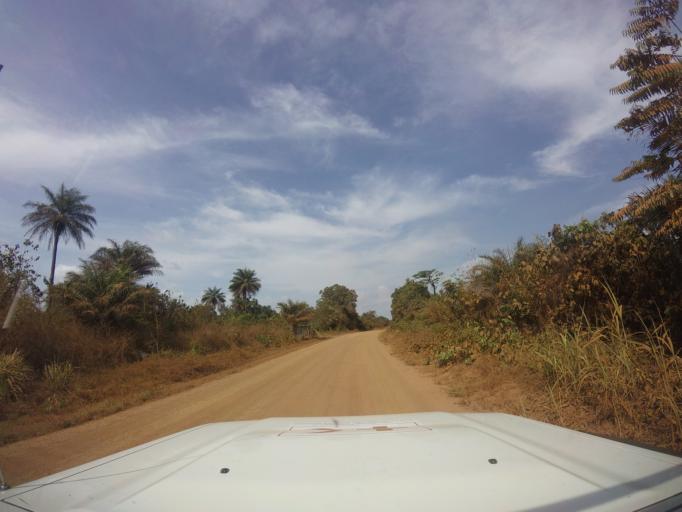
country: LR
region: Grand Cape Mount
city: Robertsport
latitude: 6.6800
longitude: -11.1354
